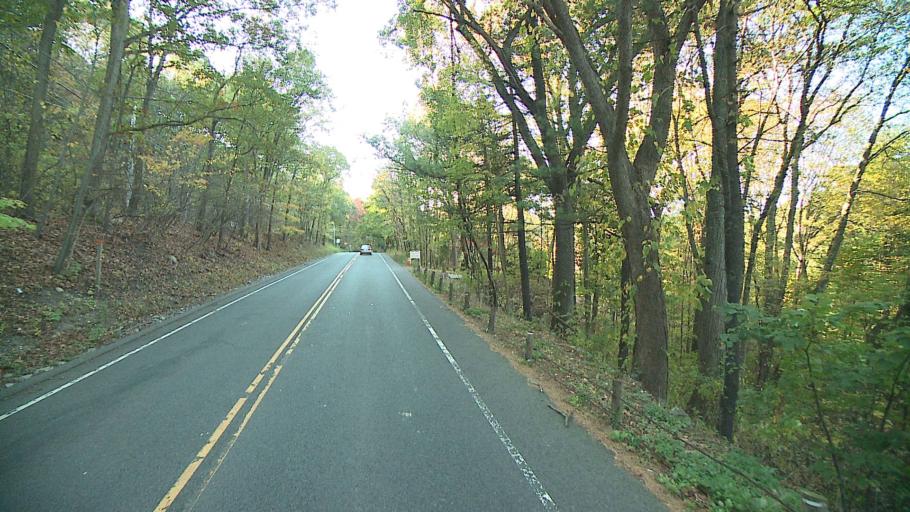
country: US
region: Connecticut
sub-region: Fairfield County
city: Bethel
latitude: 41.3511
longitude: -73.4140
